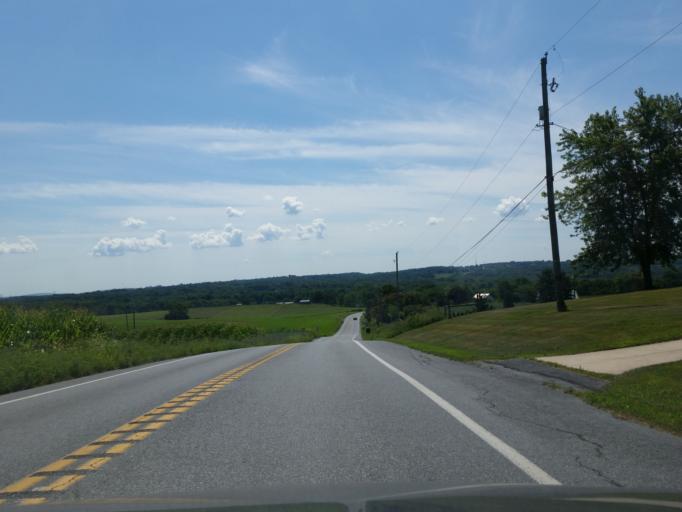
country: US
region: Pennsylvania
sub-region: Lebanon County
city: Palmyra
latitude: 40.3643
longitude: -76.6254
